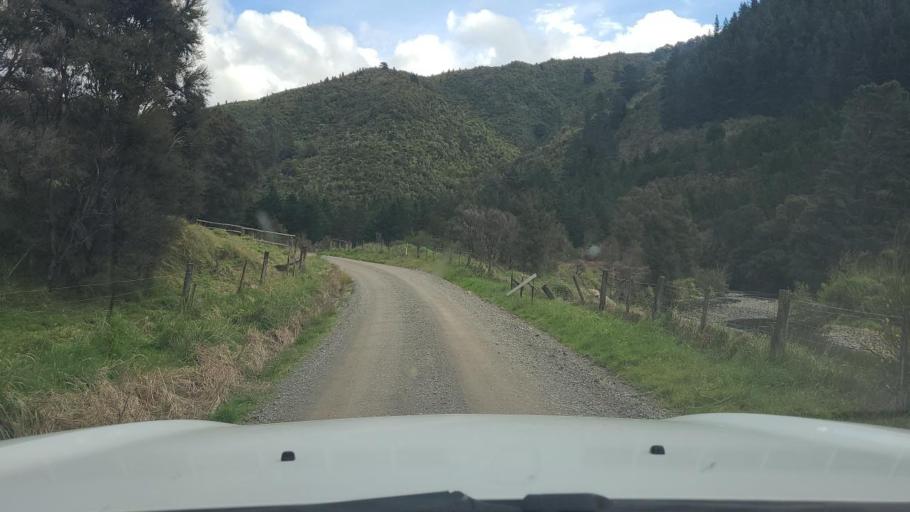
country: NZ
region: Wellington
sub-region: Masterton District
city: Masterton
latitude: -40.9348
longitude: 175.4713
